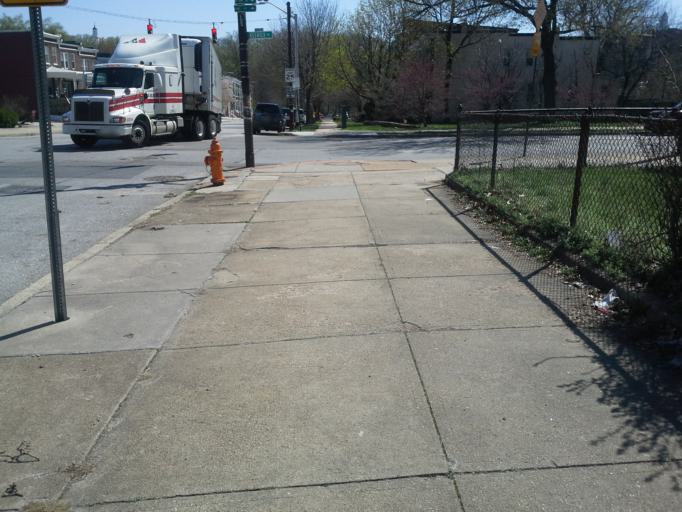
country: US
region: Maryland
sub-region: City of Baltimore
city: Baltimore
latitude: 39.3270
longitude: -76.6281
